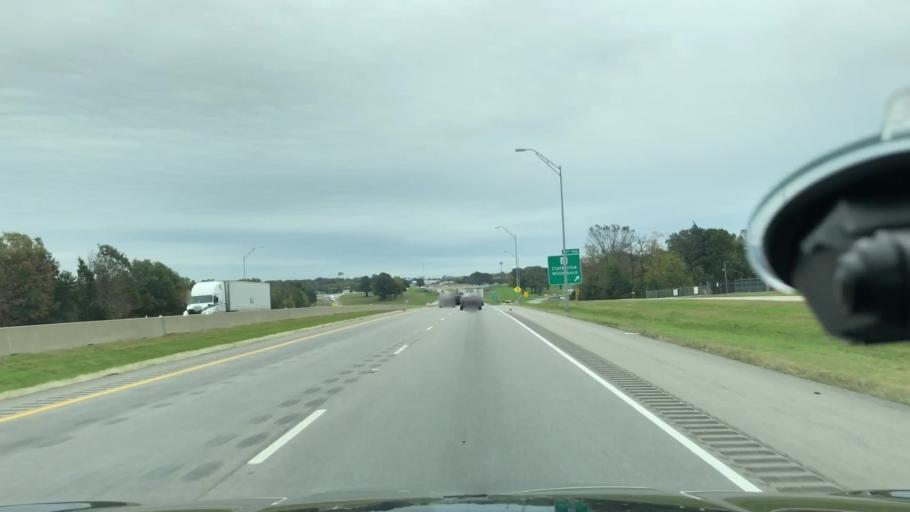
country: US
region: Texas
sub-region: Franklin County
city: Mount Vernon
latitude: 33.1624
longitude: -95.2441
